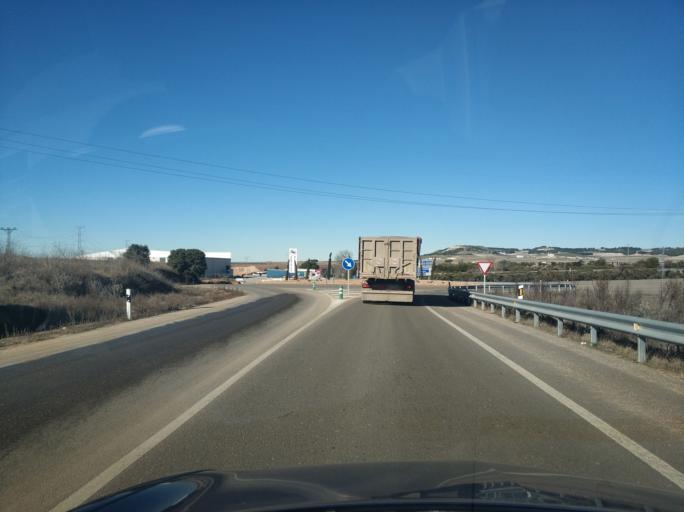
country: ES
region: Castille and Leon
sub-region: Provincia de Valladolid
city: Tordesillas
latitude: 41.5083
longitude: -5.0131
